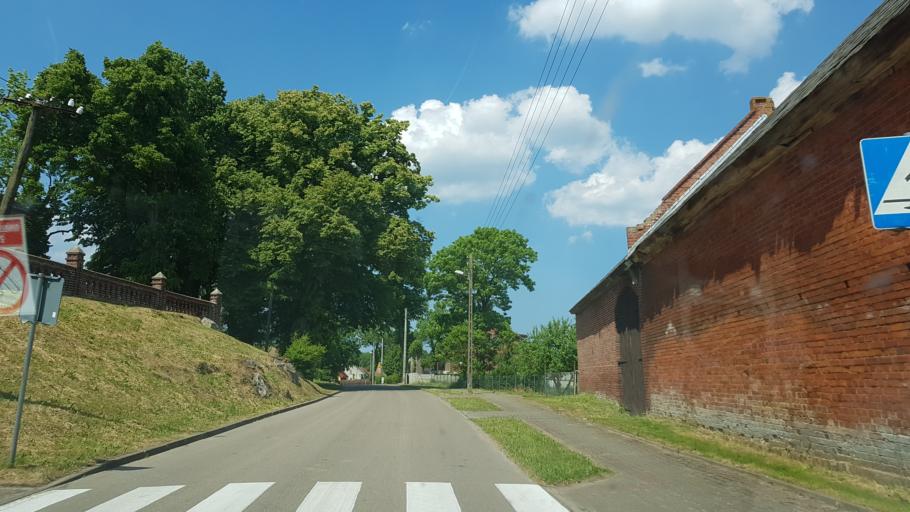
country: PL
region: West Pomeranian Voivodeship
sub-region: Powiat gryficki
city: Trzebiatow
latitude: 54.0847
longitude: 15.2135
